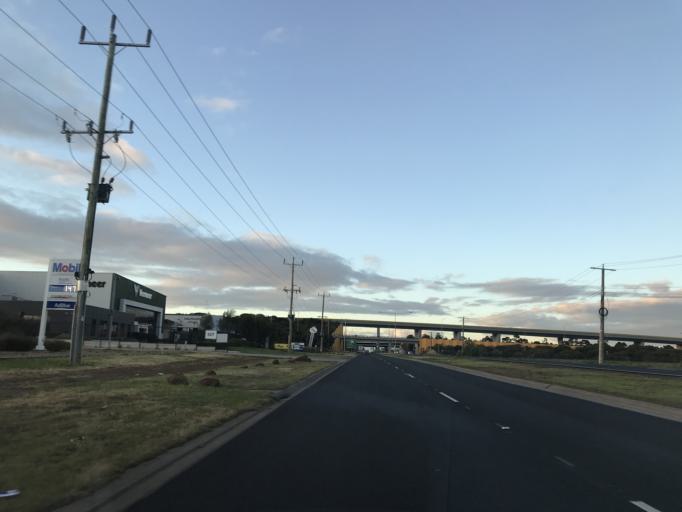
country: AU
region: Victoria
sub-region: Brimbank
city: Derrimut
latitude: -37.8027
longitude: 144.7887
